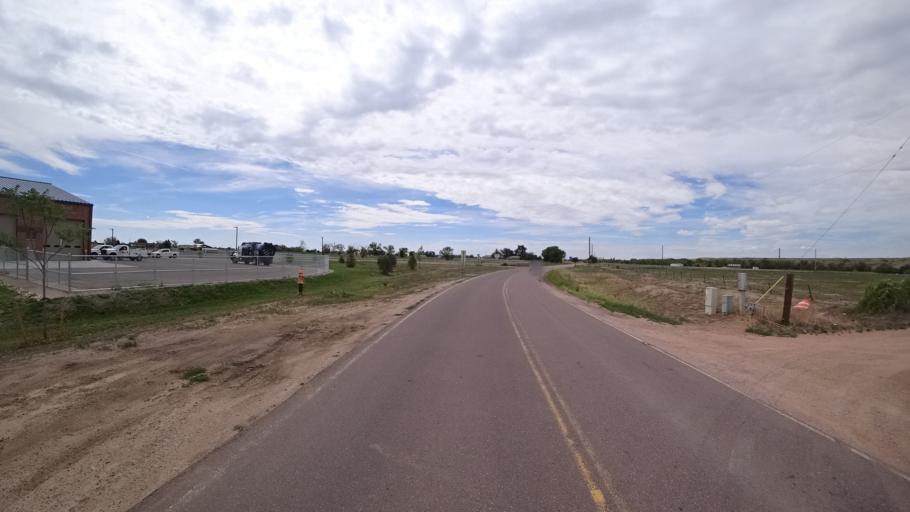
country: US
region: Colorado
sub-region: El Paso County
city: Fountain
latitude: 38.6633
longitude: -104.6919
